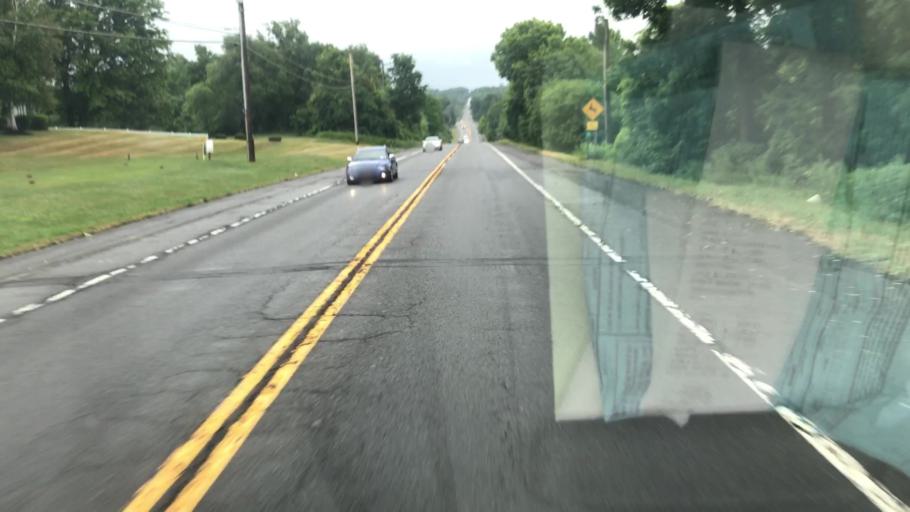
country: US
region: New York
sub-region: Onondaga County
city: Fayetteville
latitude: 43.0254
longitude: -76.0386
